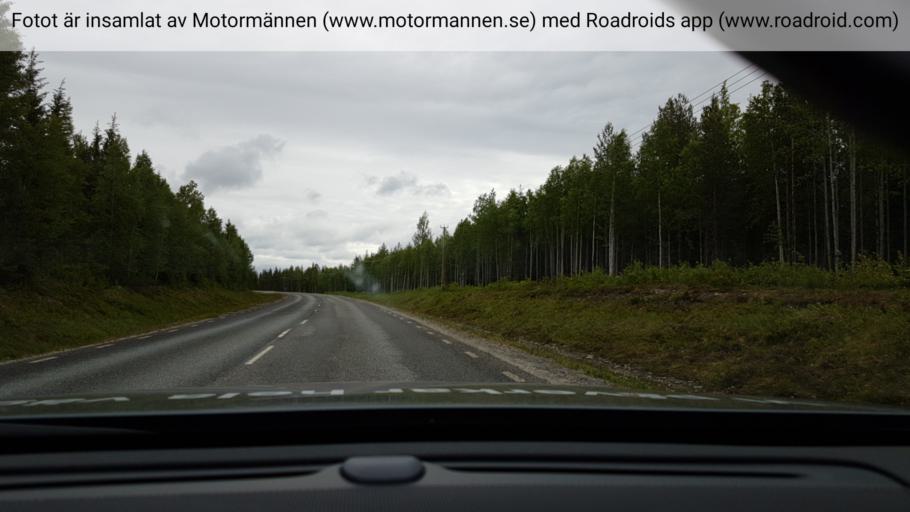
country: SE
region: Vaesterbotten
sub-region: Lycksele Kommun
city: Lycksele
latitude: 64.5376
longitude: 18.4931
